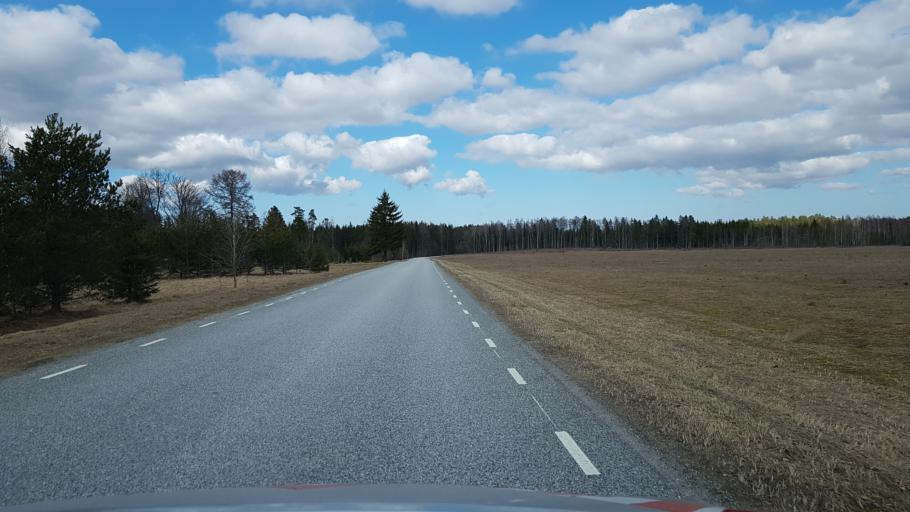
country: EE
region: Laeaene-Virumaa
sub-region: Tamsalu vald
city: Tamsalu
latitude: 59.2246
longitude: 26.1637
